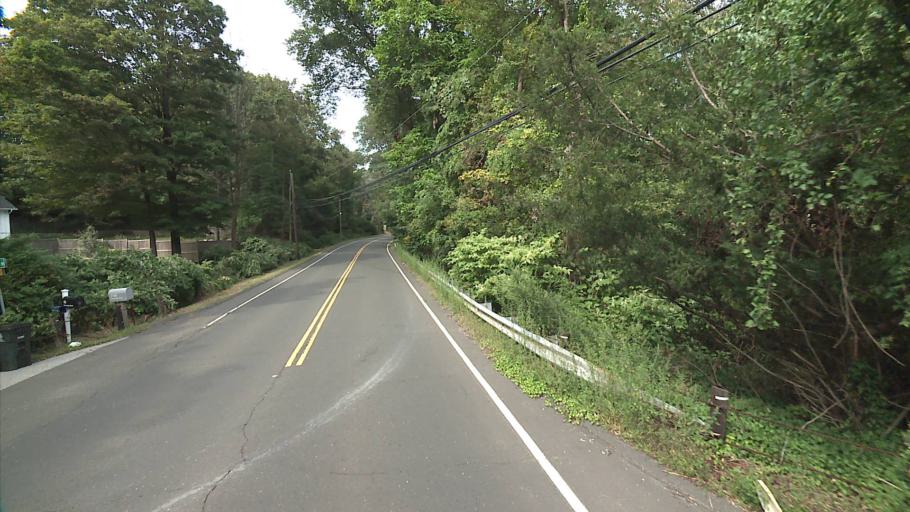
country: US
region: Connecticut
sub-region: Fairfield County
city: North Stamford
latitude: 41.1546
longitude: -73.5953
